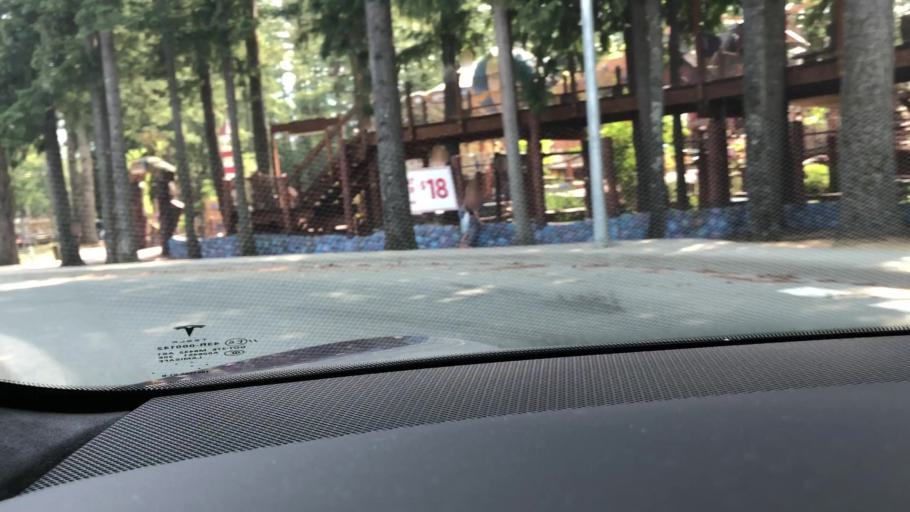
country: CA
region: British Columbia
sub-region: Fraser Valley Regional District
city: Chilliwack
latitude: 49.0751
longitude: -121.9768
